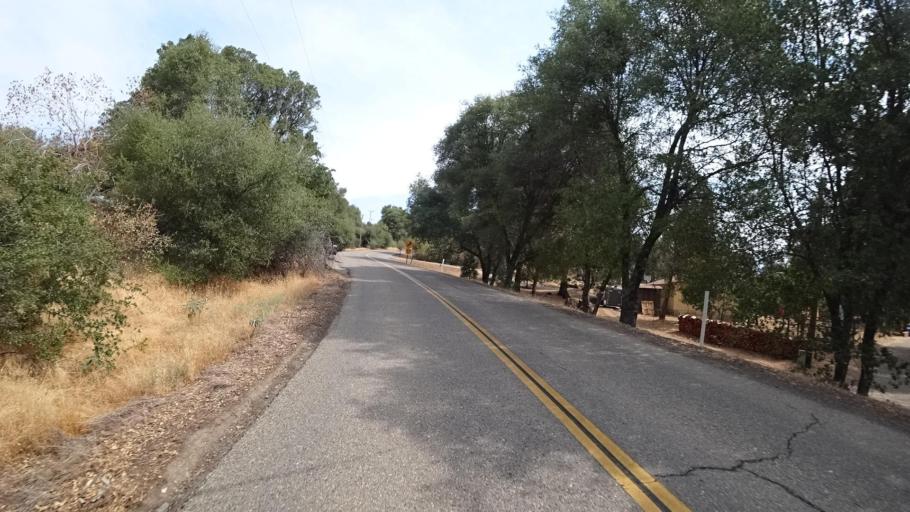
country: US
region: California
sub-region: Mariposa County
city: Midpines
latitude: 37.4993
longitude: -119.9077
